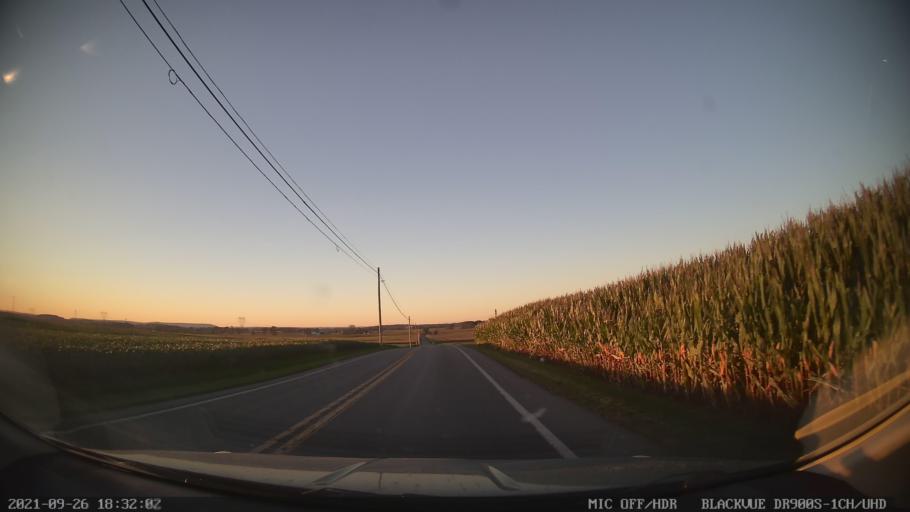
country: US
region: Pennsylvania
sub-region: Berks County
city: Kutztown
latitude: 40.4848
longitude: -75.7582
